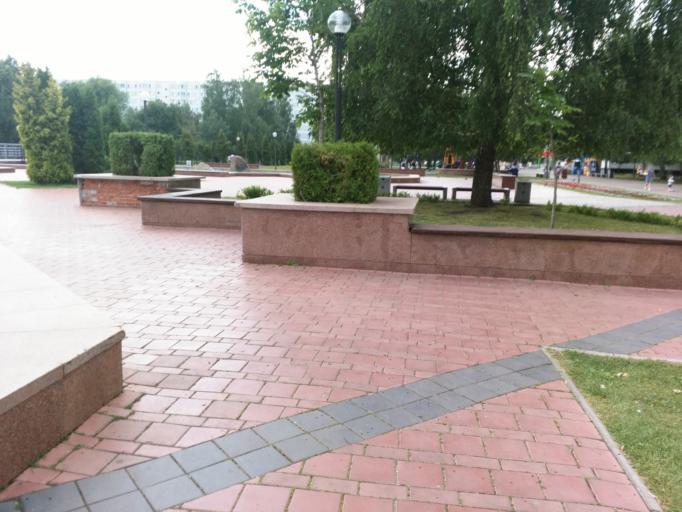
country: RU
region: Tatarstan
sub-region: Tukayevskiy Rayon
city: Naberezhnyye Chelny
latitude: 55.7429
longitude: 52.4173
